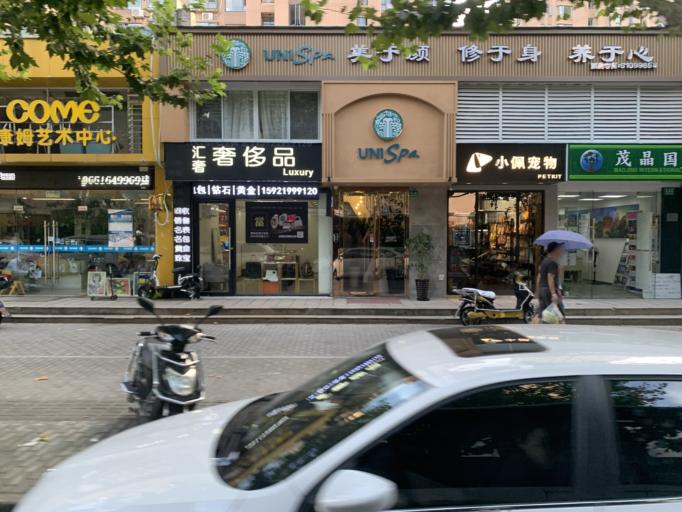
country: CN
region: Shanghai Shi
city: Huamu
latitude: 31.2067
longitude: 121.5372
